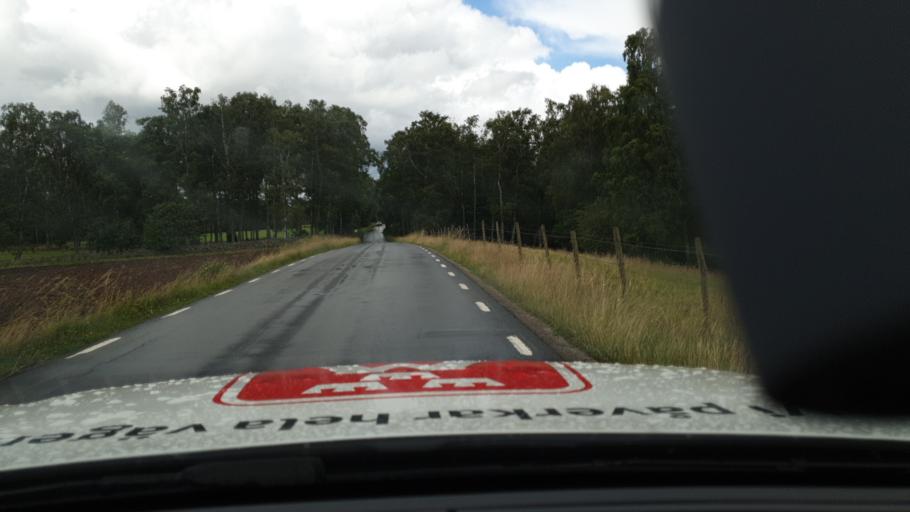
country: SE
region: Vaestra Goetaland
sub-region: Falkopings Kommun
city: Akarp
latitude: 58.2683
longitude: 13.5998
